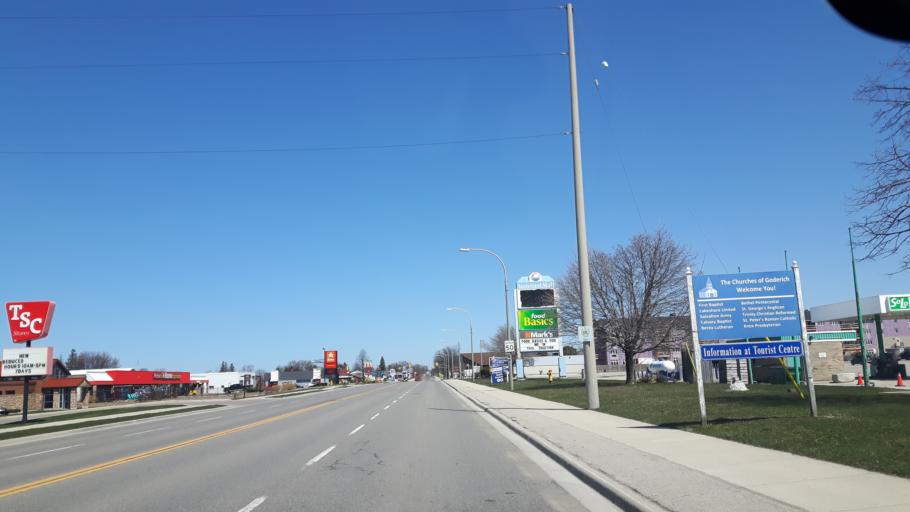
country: CA
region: Ontario
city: Goderich
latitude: 43.7289
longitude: -81.7058
